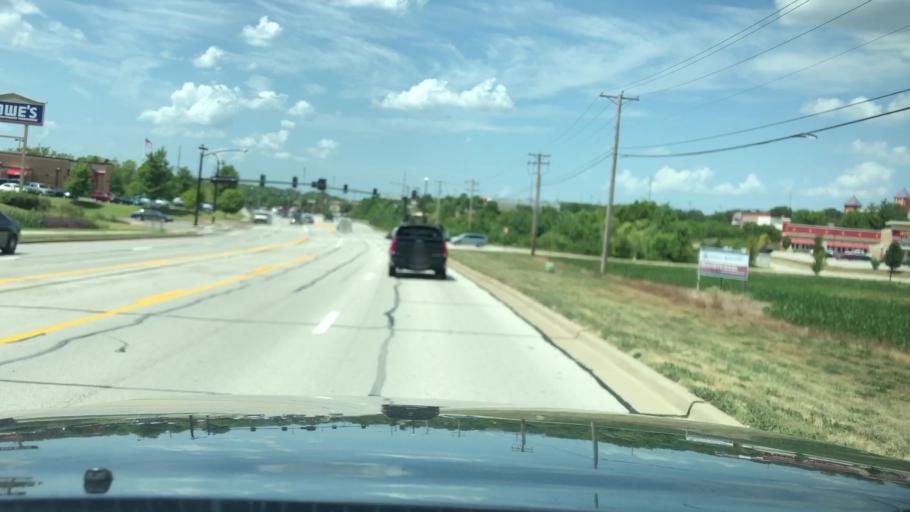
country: US
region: Missouri
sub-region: Saint Charles County
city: O'Fallon
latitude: 38.7924
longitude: -90.6951
